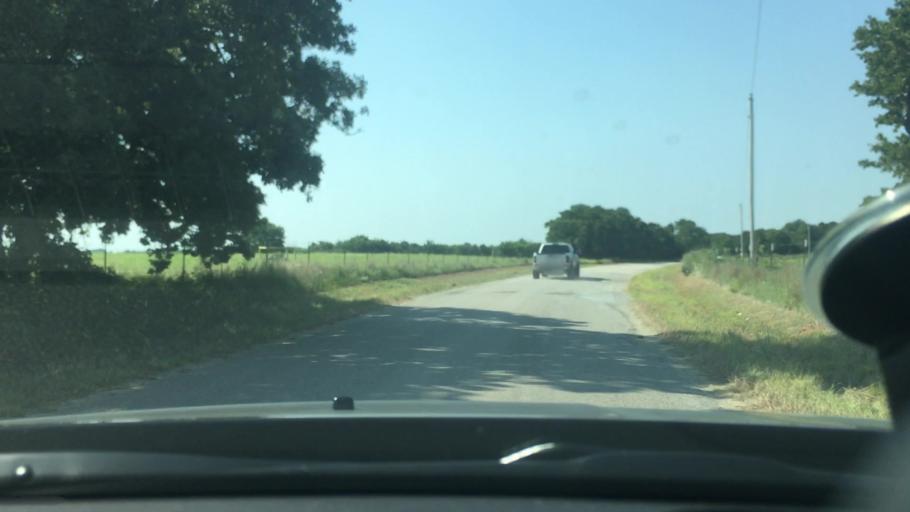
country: US
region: Oklahoma
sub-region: Garvin County
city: Lindsay
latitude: 34.7714
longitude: -97.6121
